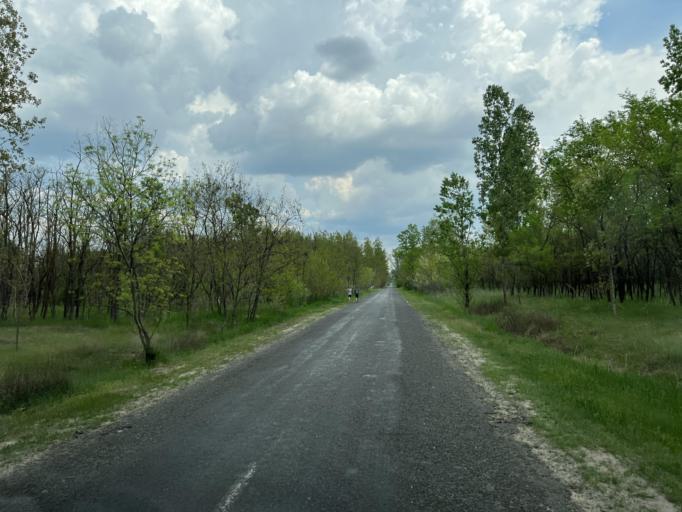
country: HU
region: Pest
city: Csemo
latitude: 47.0985
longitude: 19.7407
